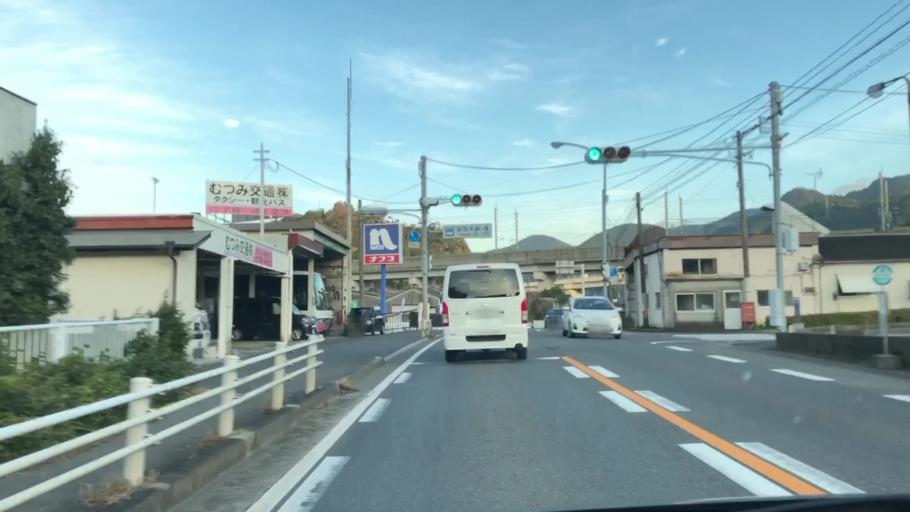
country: JP
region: Kumamoto
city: Minamata
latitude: 32.2333
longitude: 130.4499
